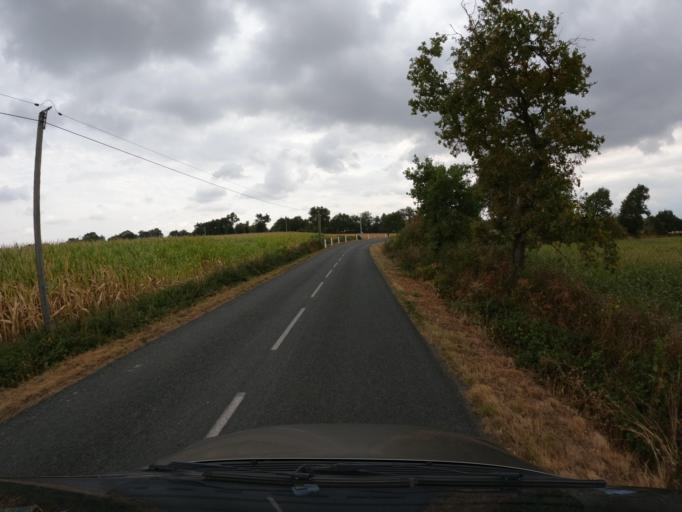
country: FR
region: Pays de la Loire
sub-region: Departement de Maine-et-Loire
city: Le Longeron
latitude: 47.0014
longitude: -1.0642
